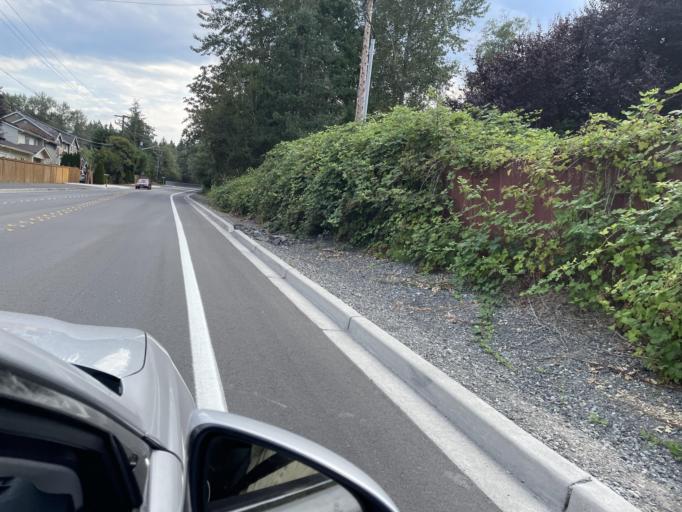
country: US
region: Washington
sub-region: King County
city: Eastgate
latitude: 47.5713
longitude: -122.1575
